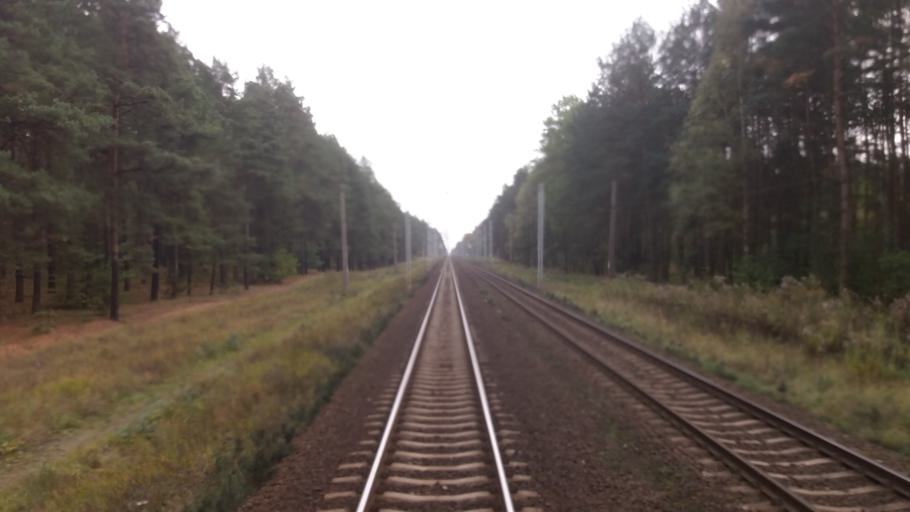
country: PL
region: West Pomeranian Voivodeship
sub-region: Powiat stargardzki
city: Kobylanka
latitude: 53.3819
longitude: 14.7754
